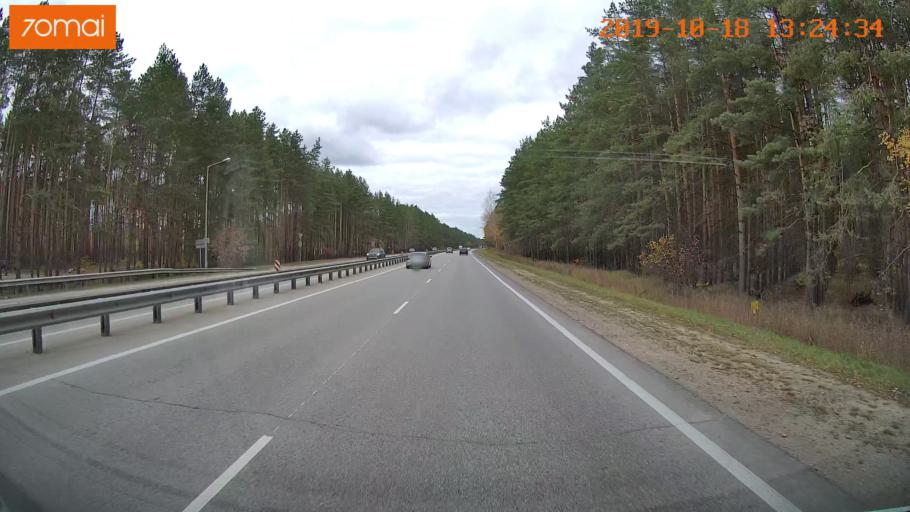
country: RU
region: Rjazan
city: Polyany
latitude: 54.7327
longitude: 39.8431
